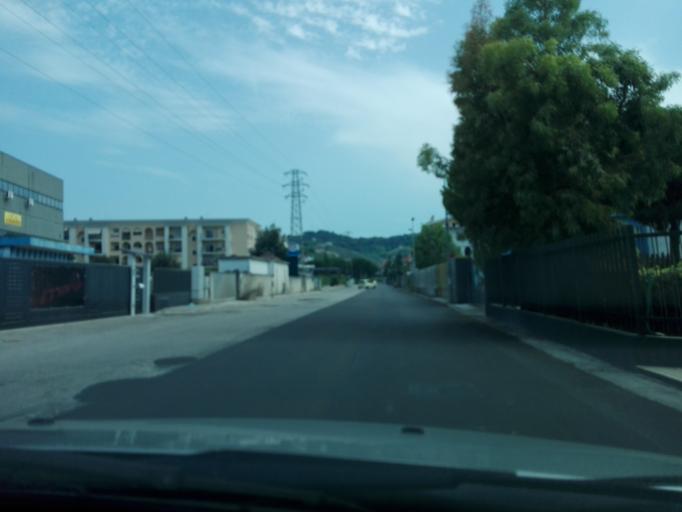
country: IT
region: Abruzzo
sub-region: Provincia di Pescara
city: Montesilvano Marina
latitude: 42.5058
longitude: 14.1315
